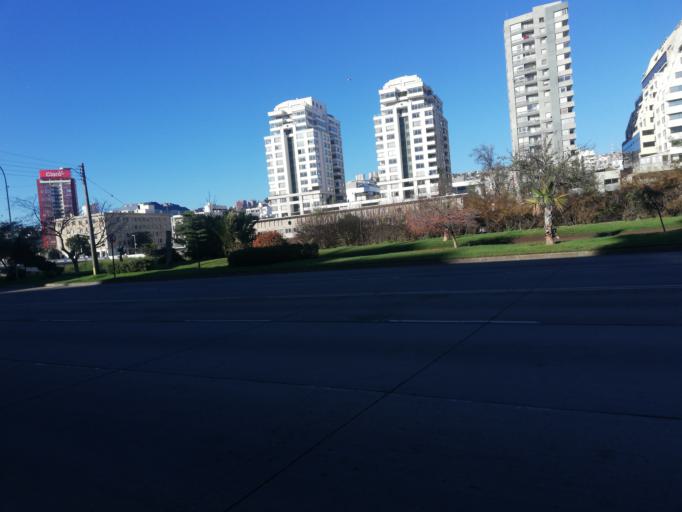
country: CL
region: Valparaiso
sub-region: Provincia de Valparaiso
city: Vina del Mar
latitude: -33.0213
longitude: -71.5580
